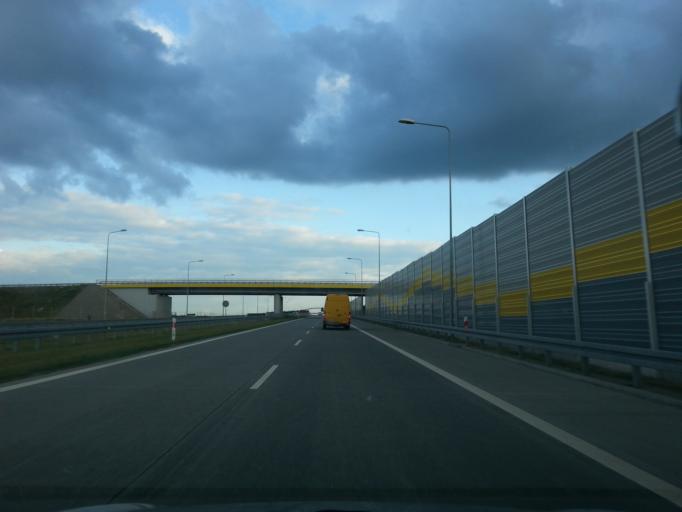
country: PL
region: Lodz Voivodeship
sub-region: Powiat sieradzki
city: Sieradz
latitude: 51.5331
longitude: 18.6964
